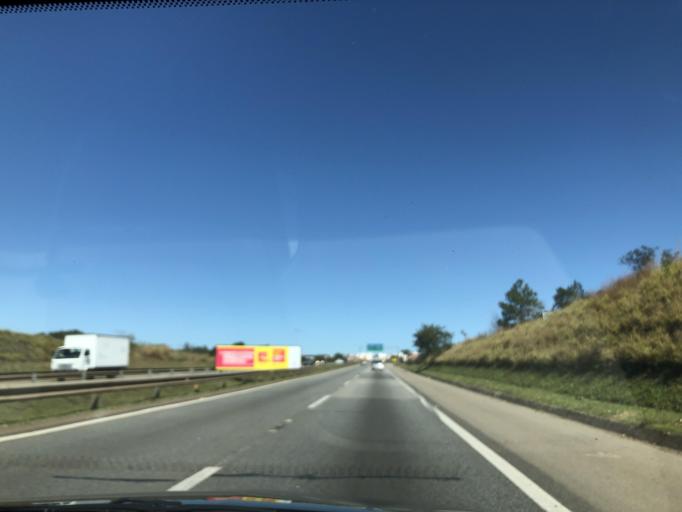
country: BR
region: Sao Paulo
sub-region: Sorocaba
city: Sorocaba
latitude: -23.4874
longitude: -47.3893
